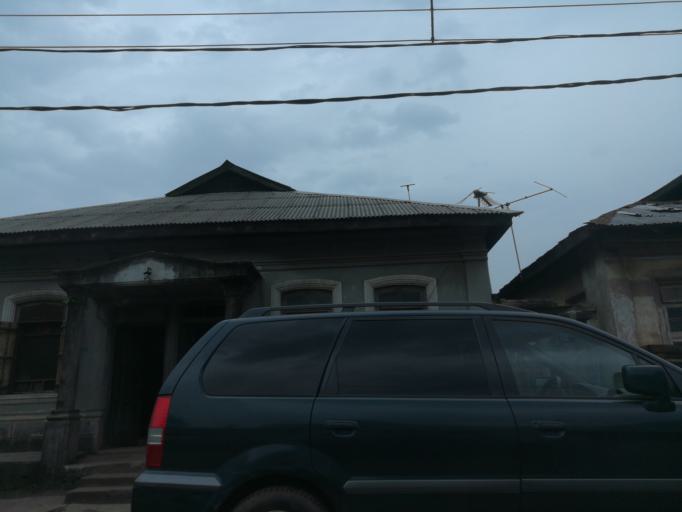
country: NG
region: Lagos
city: Ebute Metta
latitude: 6.4854
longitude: 3.3857
